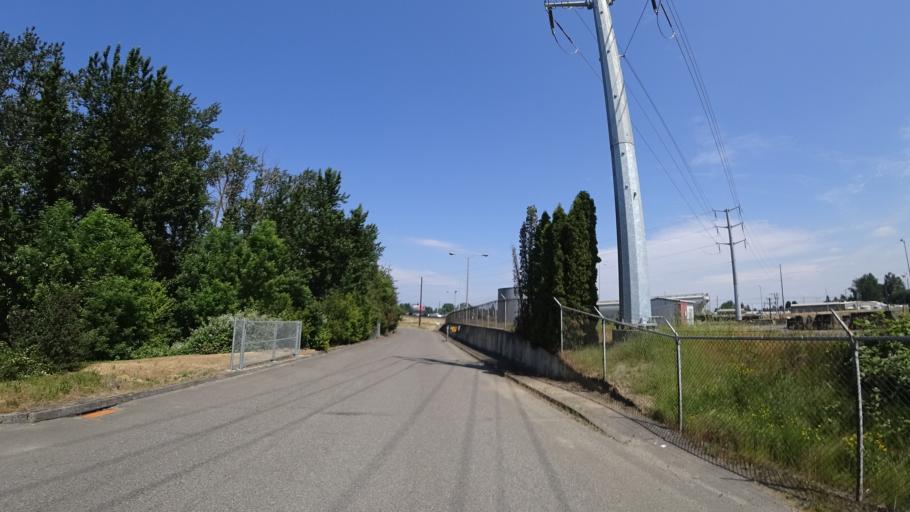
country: US
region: Oregon
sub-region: Multnomah County
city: Lents
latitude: 45.5636
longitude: -122.5617
